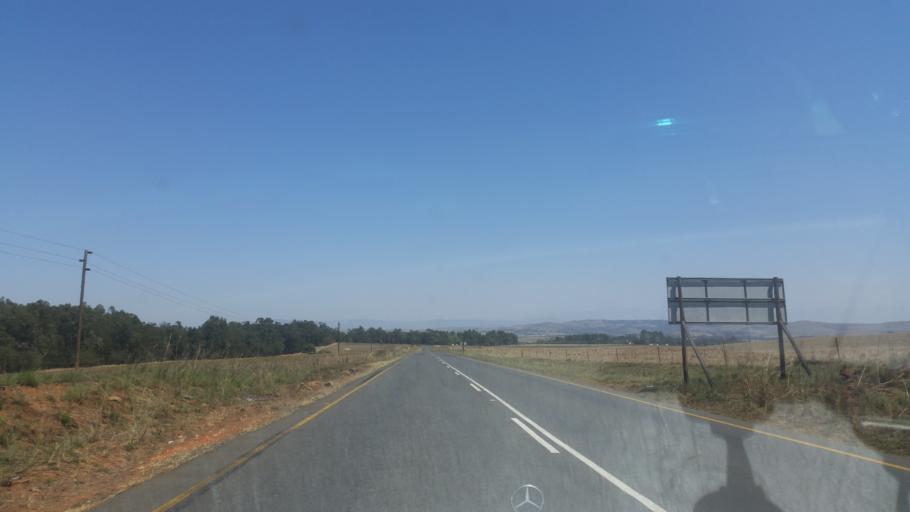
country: ZA
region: KwaZulu-Natal
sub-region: uMgungundlovu District Municipality
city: Mooirivier
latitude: -29.1442
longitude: 29.9925
